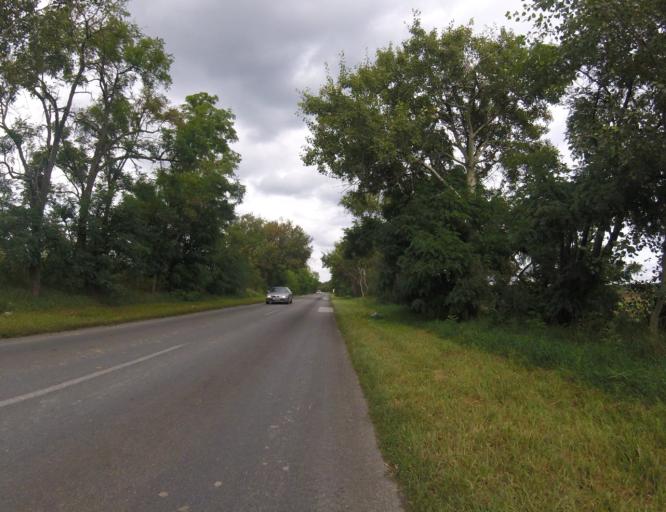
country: HU
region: Pest
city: Szigetcsep
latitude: 47.2834
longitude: 18.9818
